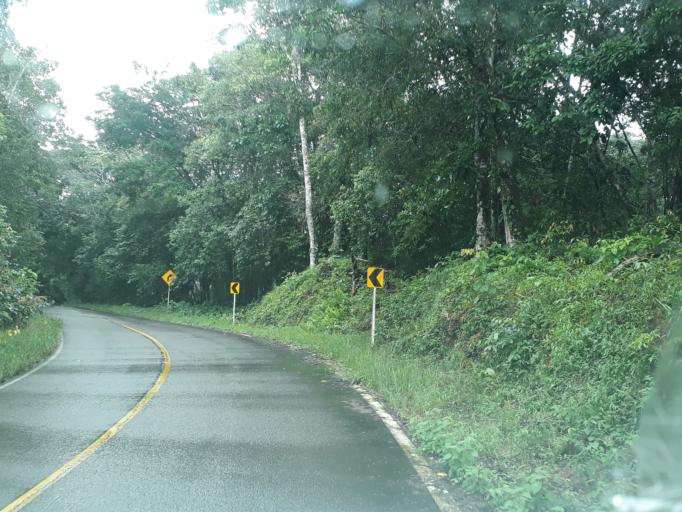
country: CO
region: Cundinamarca
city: Medina
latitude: 4.4531
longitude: -73.3244
